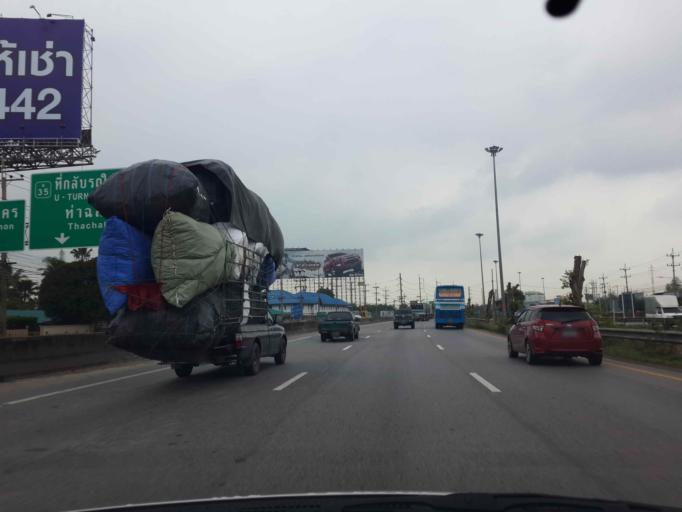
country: TH
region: Samut Sakhon
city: Samut Sakhon
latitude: 13.5459
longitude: 100.2586
